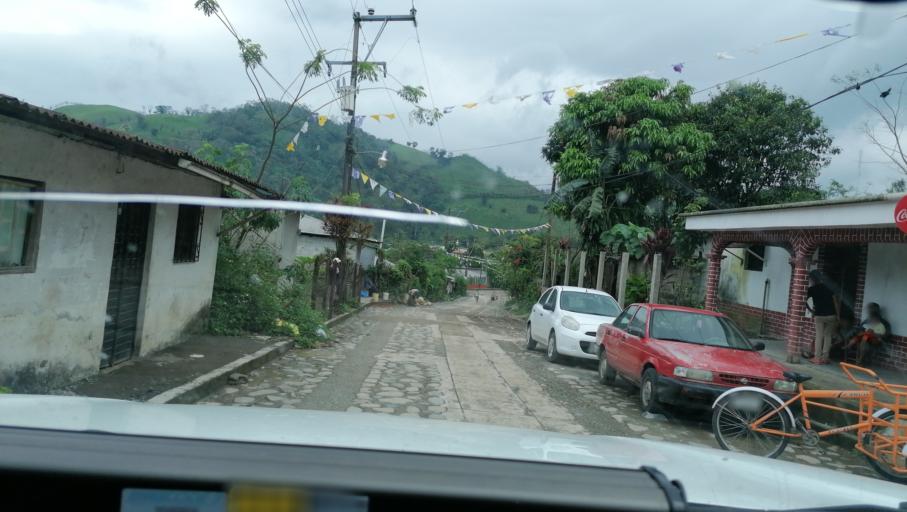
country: MX
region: Chiapas
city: Ixtacomitan
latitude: 17.3432
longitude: -93.1330
